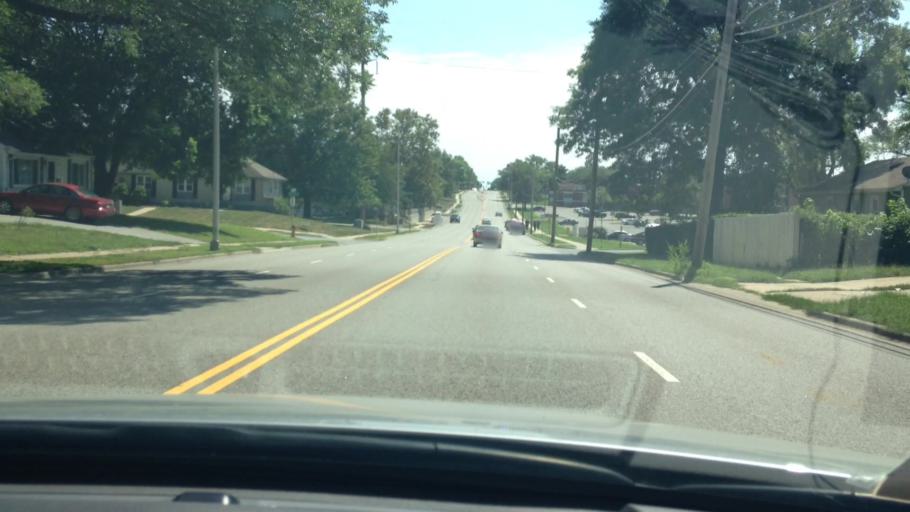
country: US
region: Kansas
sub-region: Johnson County
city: Overland Park
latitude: 38.9792
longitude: -94.6864
